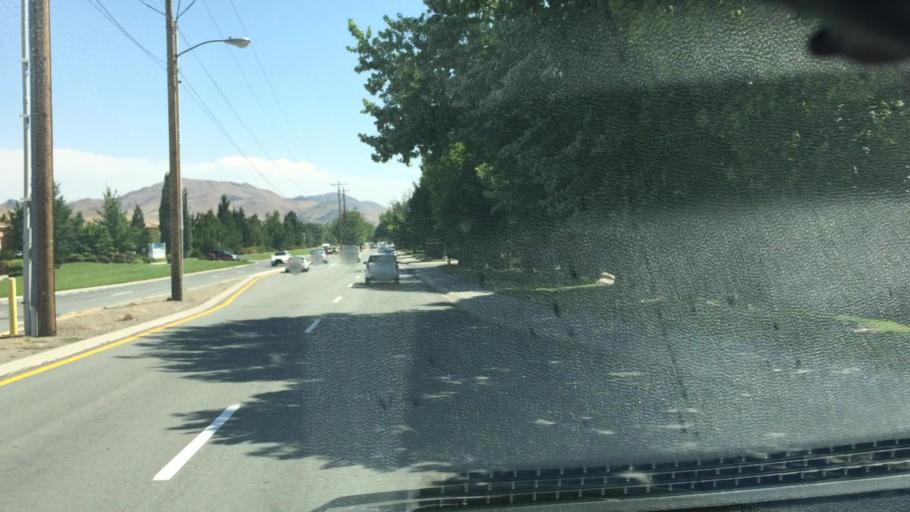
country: US
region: Nevada
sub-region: Washoe County
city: Sparks
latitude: 39.5564
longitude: -119.7057
